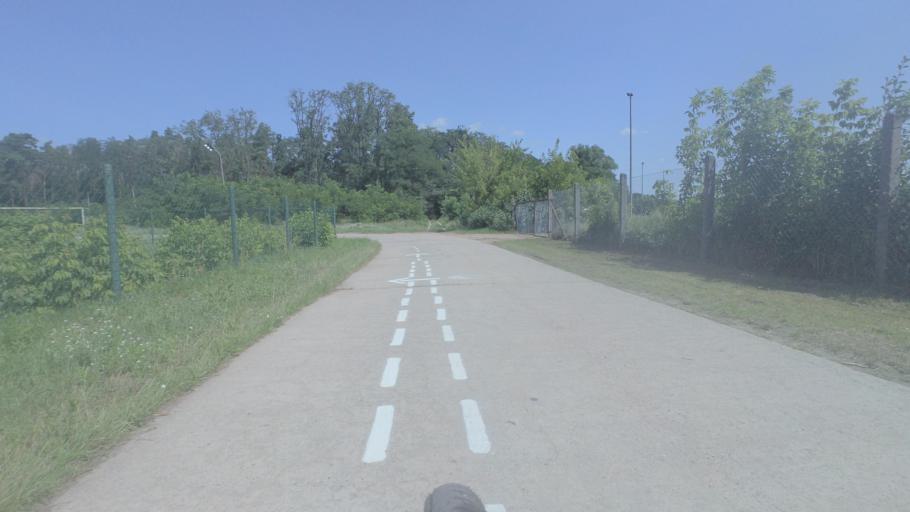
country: DE
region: Brandenburg
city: Rangsdorf
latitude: 52.2569
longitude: 13.3818
